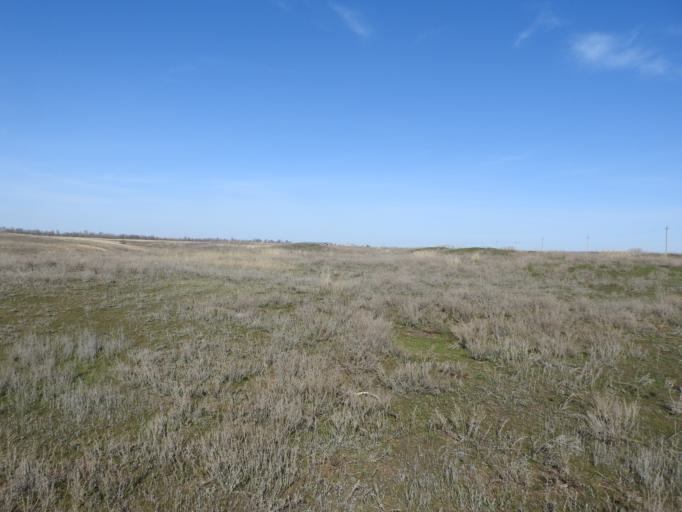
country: RU
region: Volgograd
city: Staraya Poltavka
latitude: 50.7774
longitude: 46.4129
